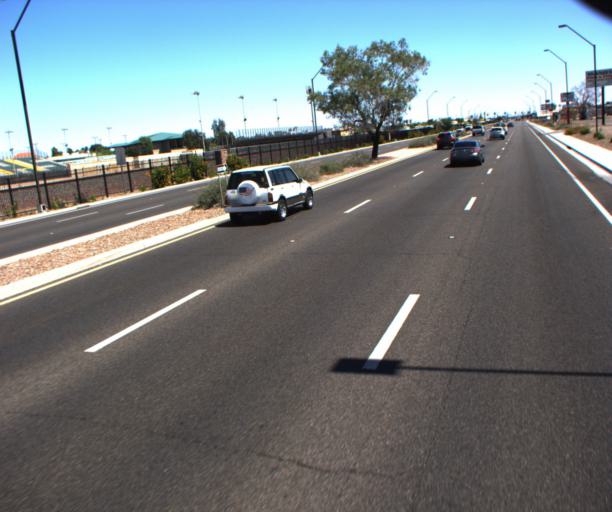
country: US
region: Arizona
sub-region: Maricopa County
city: Peoria
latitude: 33.5871
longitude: -112.2445
